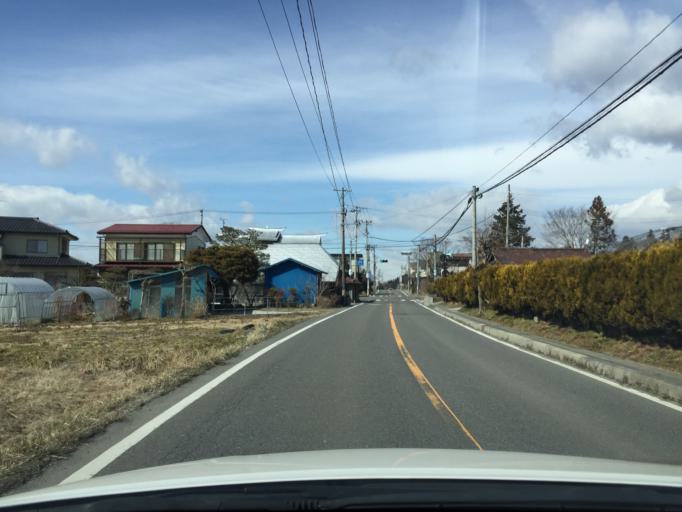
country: JP
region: Fukushima
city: Funehikimachi-funehiki
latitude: 37.3977
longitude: 140.5684
